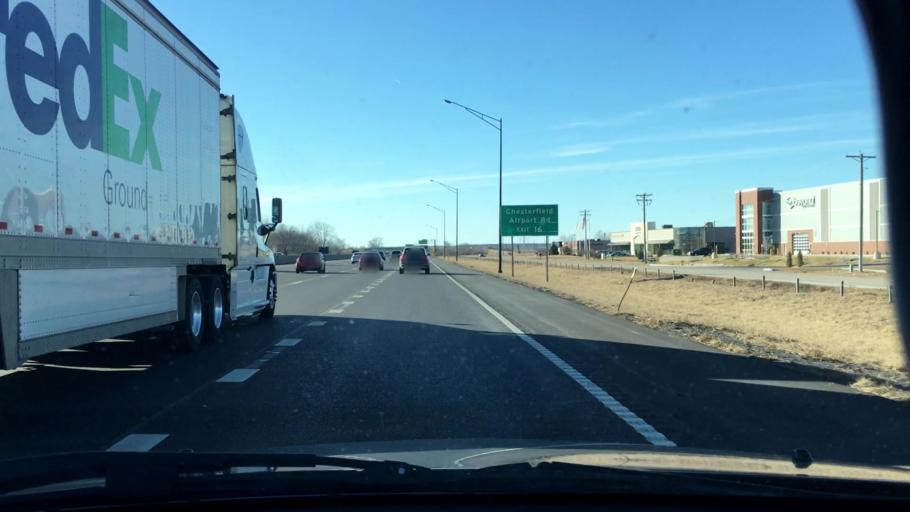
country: US
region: Missouri
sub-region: Saint Louis County
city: Chesterfield
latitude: 38.6714
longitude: -90.6063
